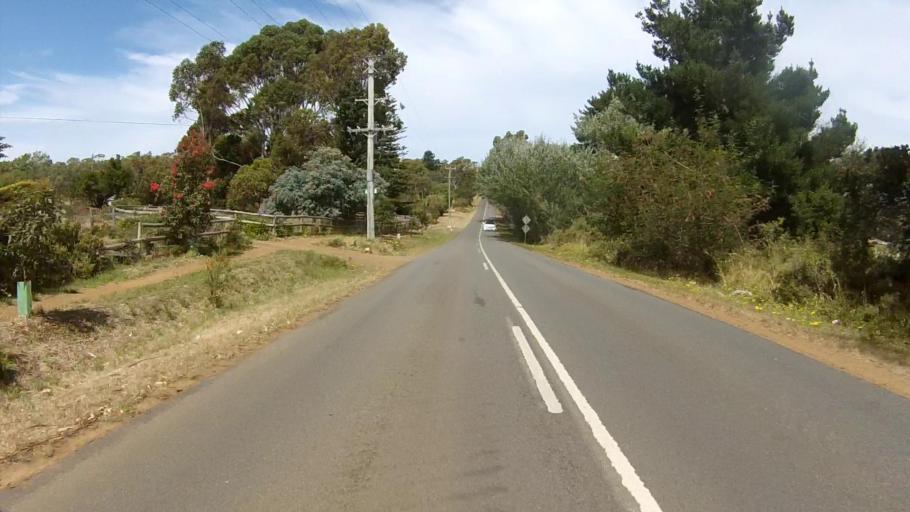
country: AU
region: Tasmania
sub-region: Kingborough
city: Taroona
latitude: -43.0127
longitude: 147.4140
